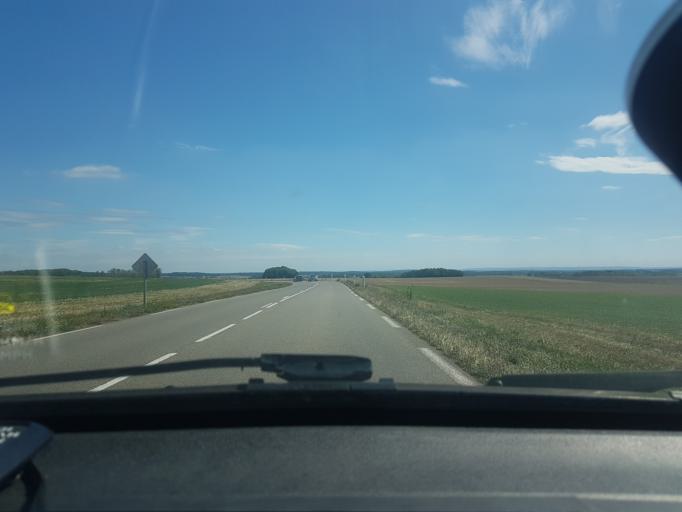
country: FR
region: Bourgogne
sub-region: Departement de la Cote-d'Or
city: Mirebeau-sur-Beze
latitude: 47.3825
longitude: 5.2927
